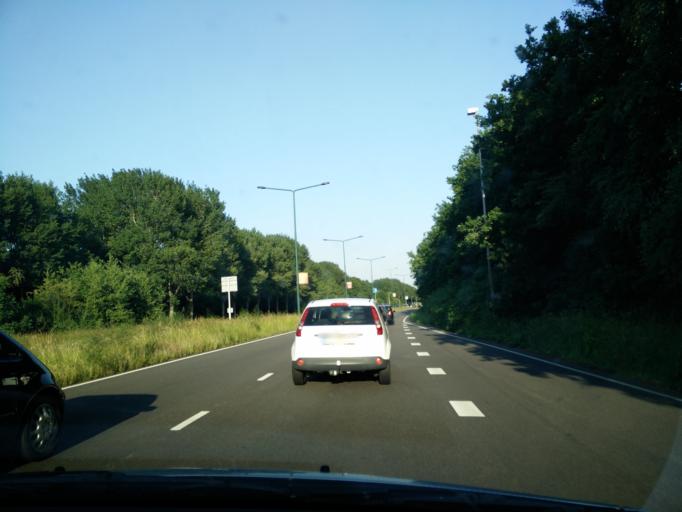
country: NL
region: North Brabant
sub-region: Gemeente Breda
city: Breda
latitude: 51.6021
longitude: 4.7344
